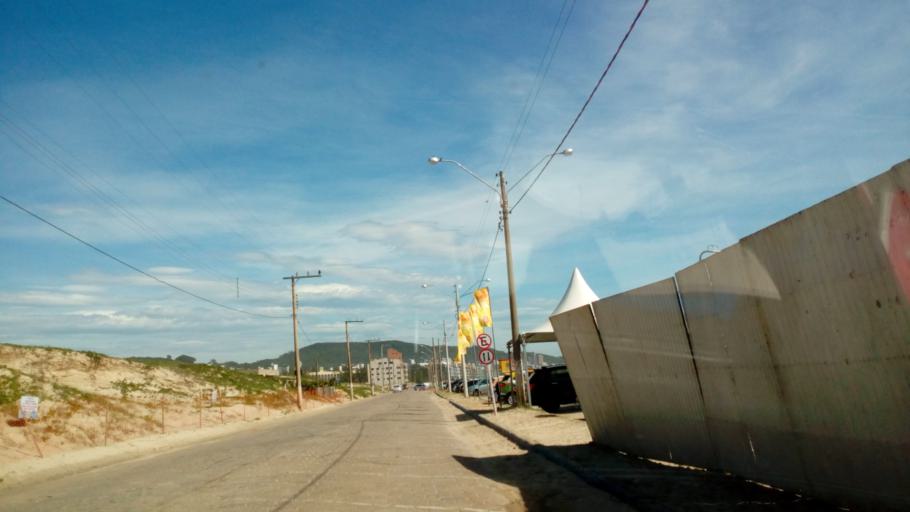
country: BR
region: Santa Catarina
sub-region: Laguna
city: Laguna
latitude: -28.4941
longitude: -48.7624
